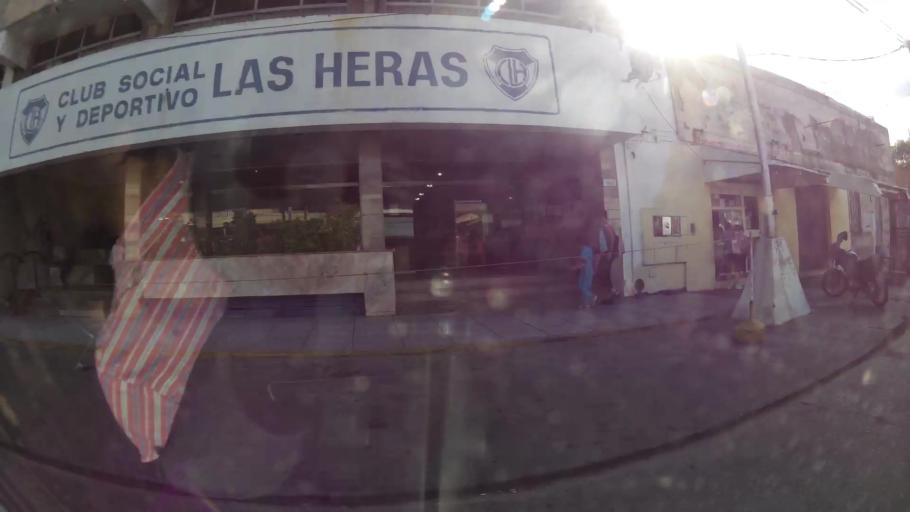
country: AR
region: Buenos Aires
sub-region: Partido de General San Martin
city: General San Martin
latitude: -34.5443
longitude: -58.5517
